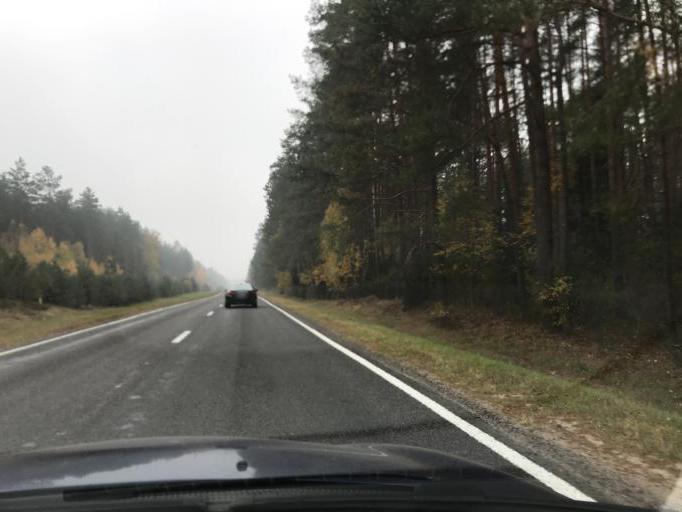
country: LT
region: Alytaus apskritis
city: Druskininkai
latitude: 53.8825
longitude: 23.9048
